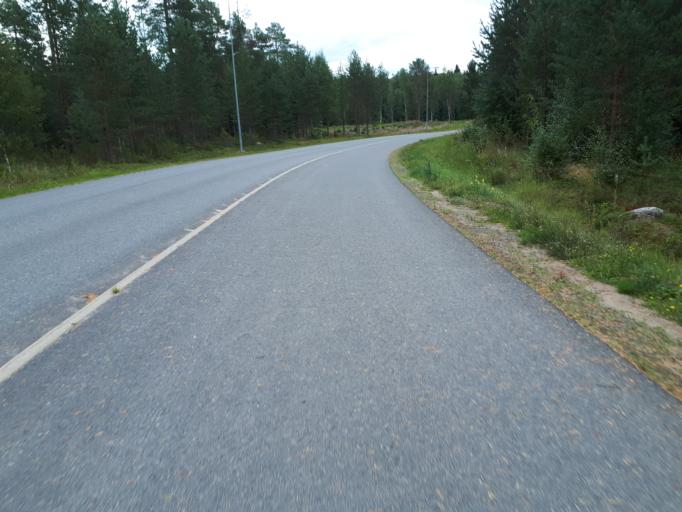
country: FI
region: Northern Ostrobothnia
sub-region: Oulunkaari
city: Ii
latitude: 65.3241
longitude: 25.4098
